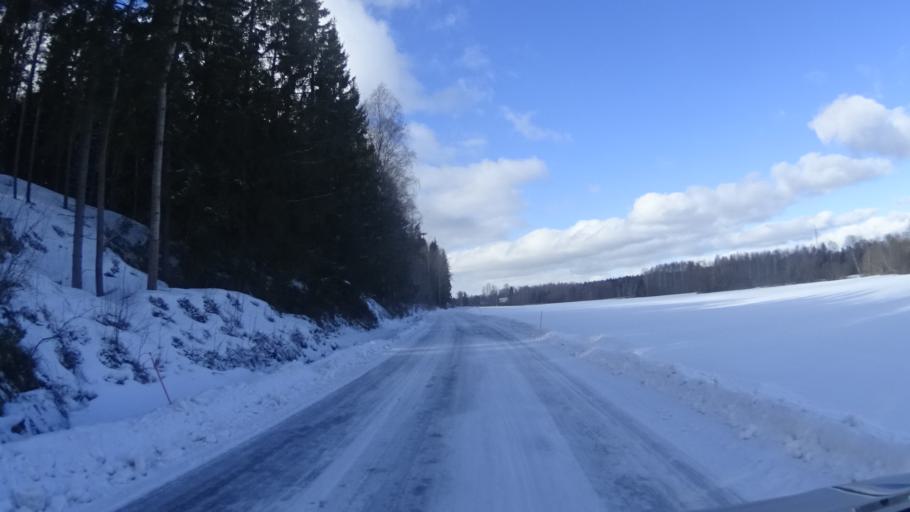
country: FI
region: Uusimaa
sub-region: Helsinki
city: Vantaa
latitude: 60.2459
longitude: 25.1734
